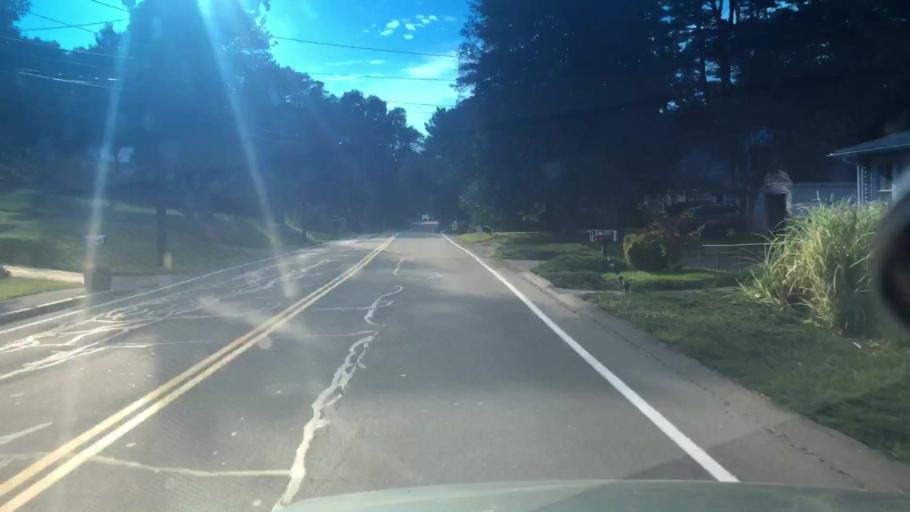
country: US
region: Massachusetts
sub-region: Norfolk County
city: Walpole
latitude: 42.1496
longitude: -71.2615
